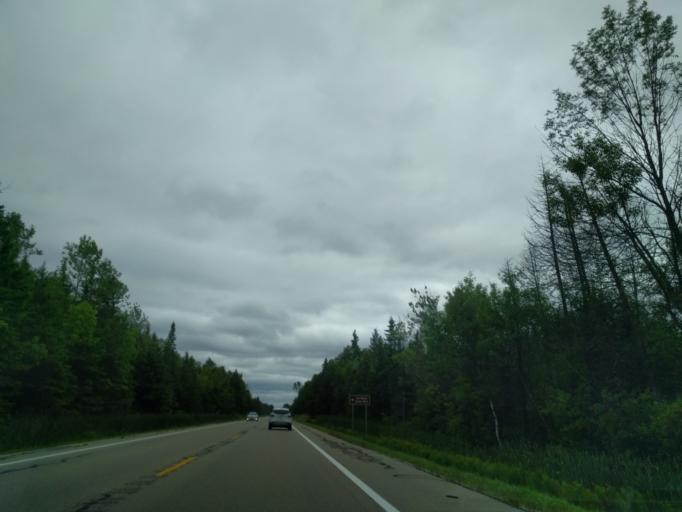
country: US
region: Michigan
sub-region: Menominee County
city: Menominee
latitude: 45.3987
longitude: -87.3655
